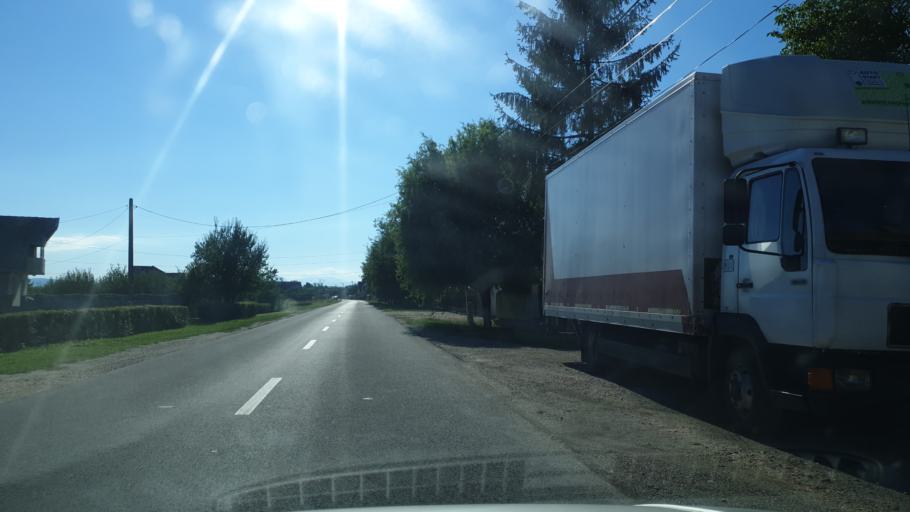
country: RO
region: Covasna
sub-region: Comuna Ilieni
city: Ilieni
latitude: 45.7650
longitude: 25.7293
